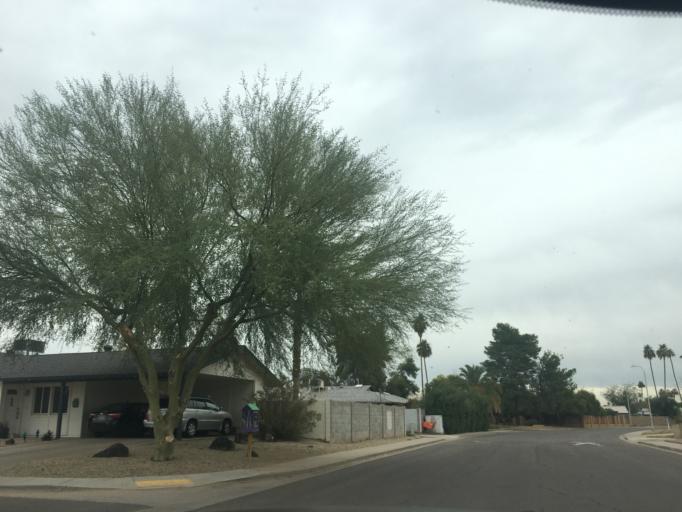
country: US
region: Arizona
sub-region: Maricopa County
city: Tempe
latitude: 33.3840
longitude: -111.9211
